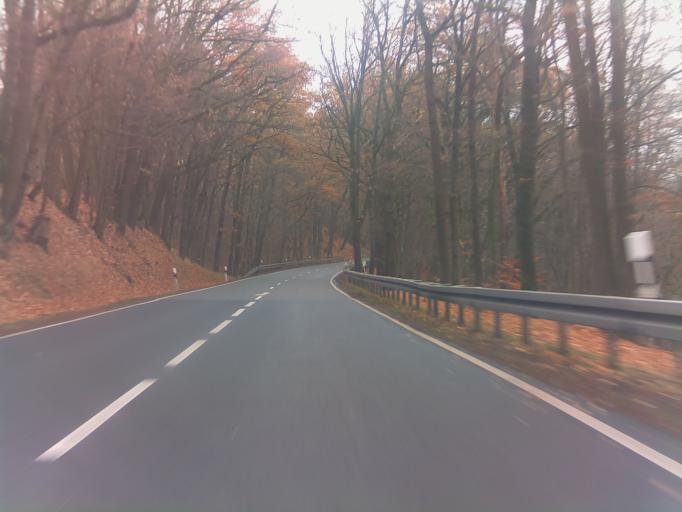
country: DE
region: Thuringia
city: Schleusingen
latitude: 50.5016
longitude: 10.7679
